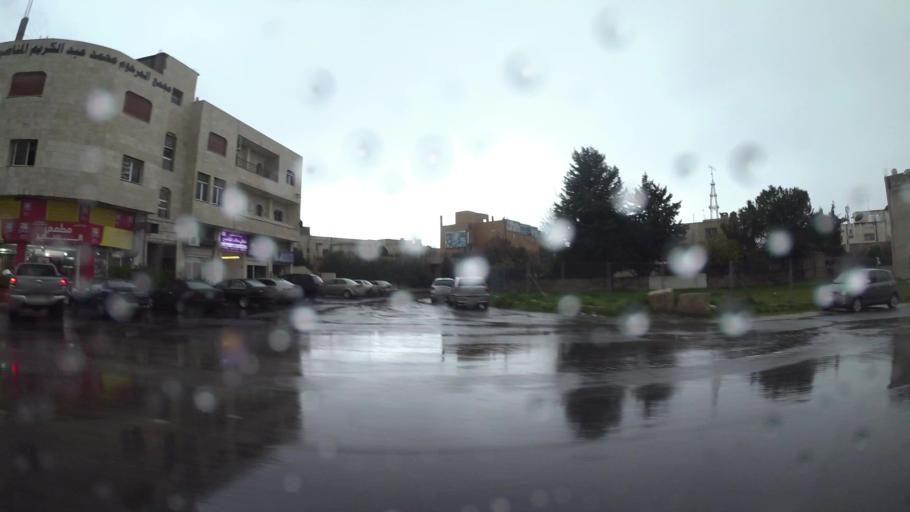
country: JO
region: Amman
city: Umm as Summaq
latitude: 31.8996
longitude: 35.8570
